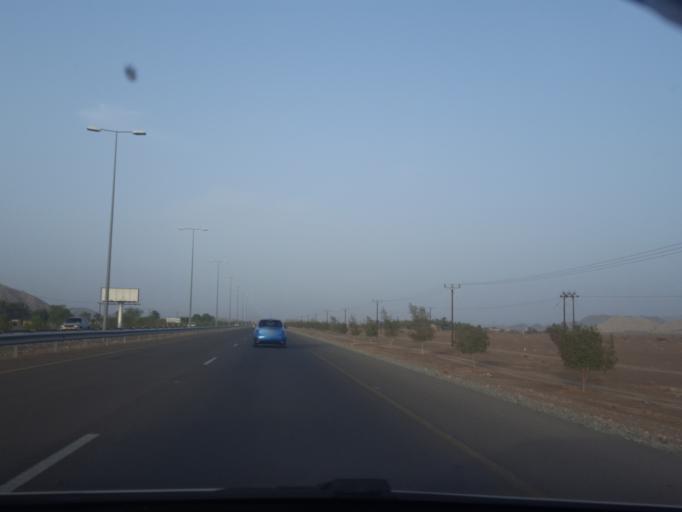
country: OM
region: Al Buraimi
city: Al Buraymi
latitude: 24.2413
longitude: 55.9725
